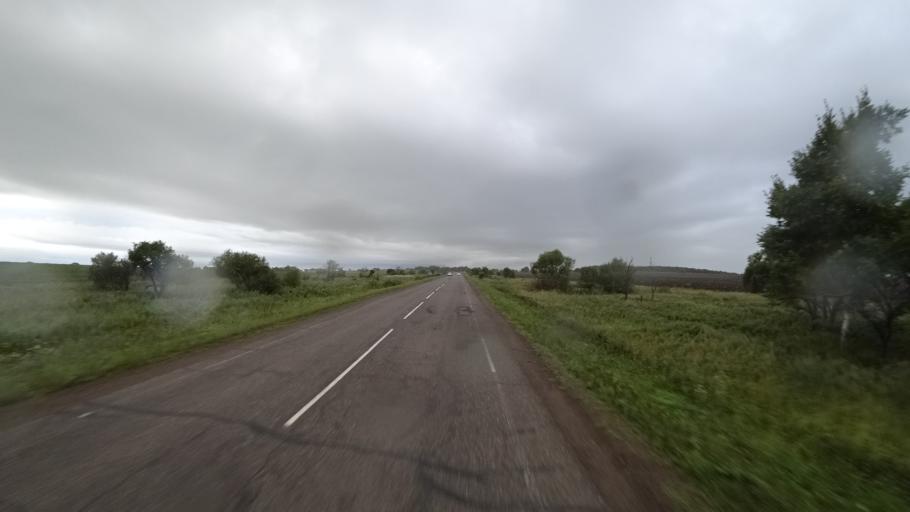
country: RU
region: Primorskiy
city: Chernigovka
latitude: 44.3640
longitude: 132.5446
